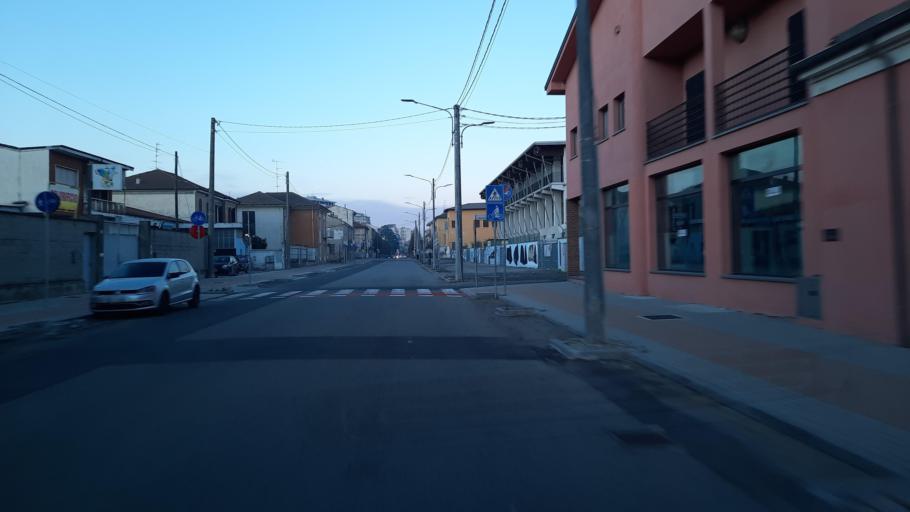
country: IT
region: Piedmont
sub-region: Provincia di Vercelli
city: Trino
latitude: 45.1882
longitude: 8.2961
